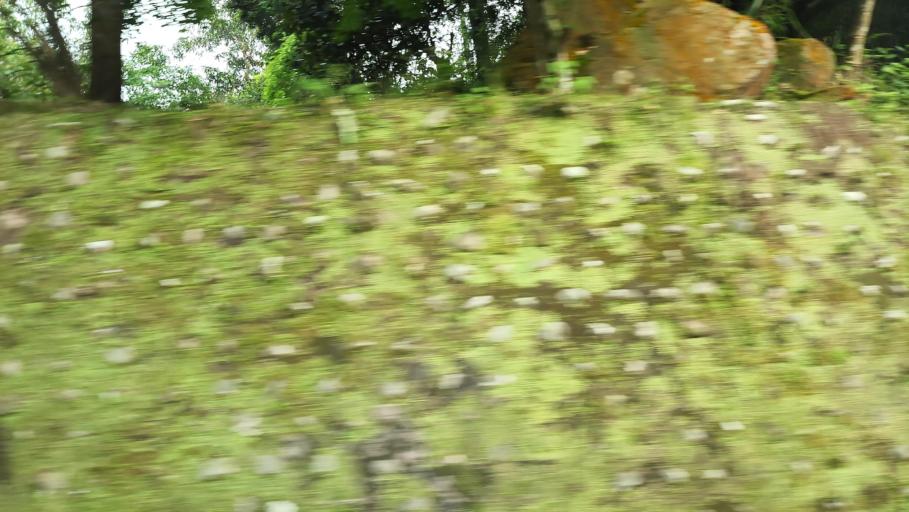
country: TW
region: Taiwan
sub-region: Keelung
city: Keelung
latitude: 25.1488
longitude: 121.6208
